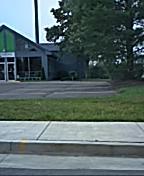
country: US
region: Kentucky
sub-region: Jefferson County
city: Douglass Hills
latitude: 38.2453
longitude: -85.5629
